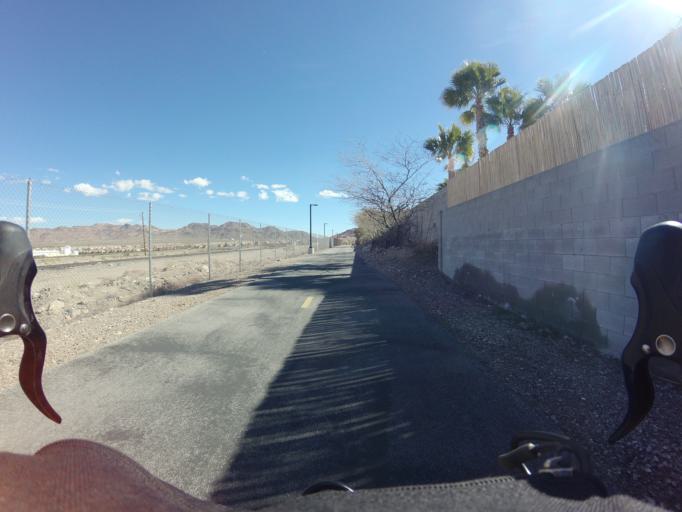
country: US
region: Nevada
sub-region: Clark County
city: Henderson
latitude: 35.9900
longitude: -114.9388
